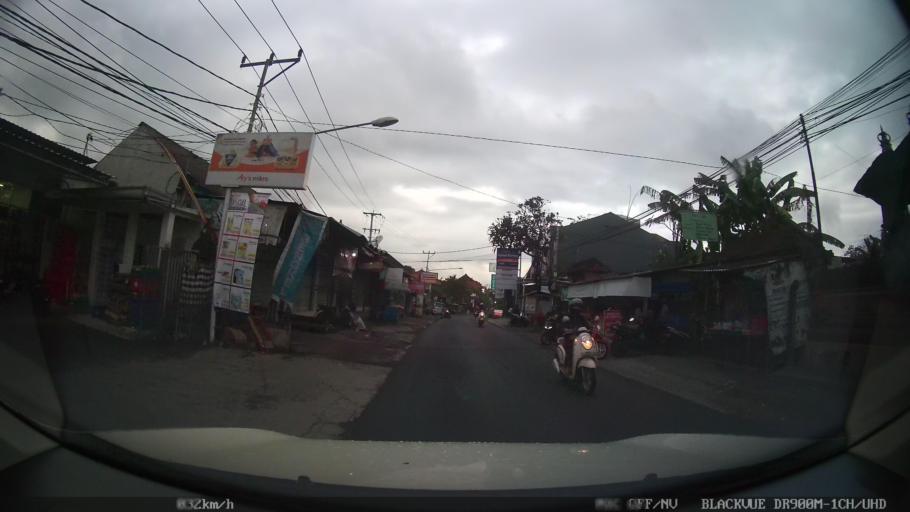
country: ID
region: Bali
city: Banjar Kertajiwa
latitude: -8.6277
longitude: 115.2627
